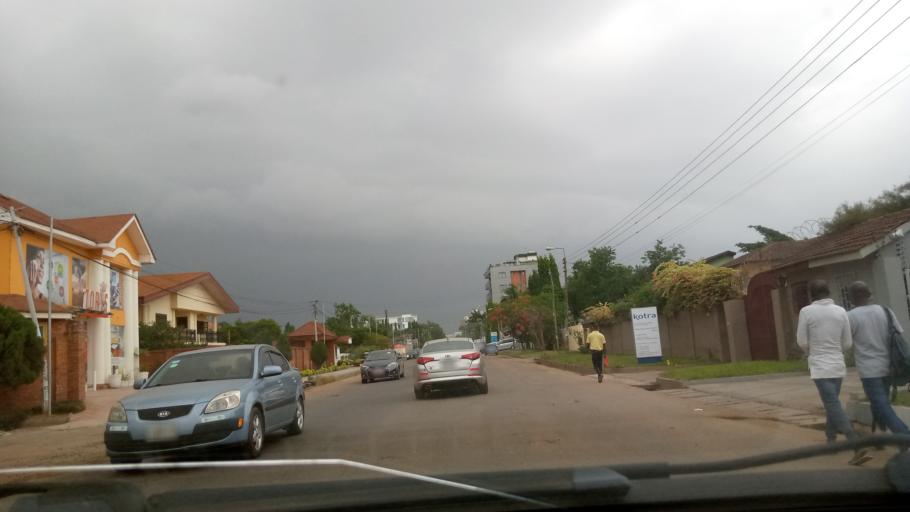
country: GH
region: Greater Accra
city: Accra
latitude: 5.6122
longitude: -0.1915
